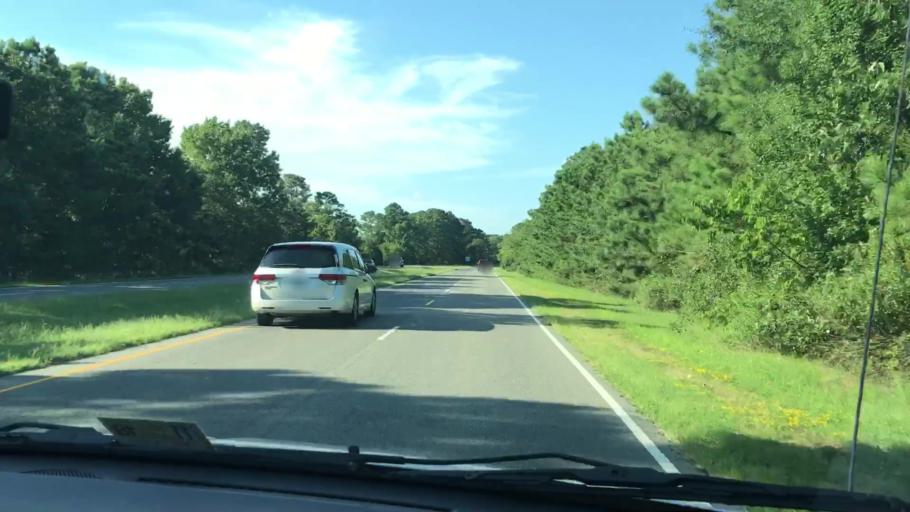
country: US
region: Virginia
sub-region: City of Hampton
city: Hampton
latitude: 37.0528
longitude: -76.3654
